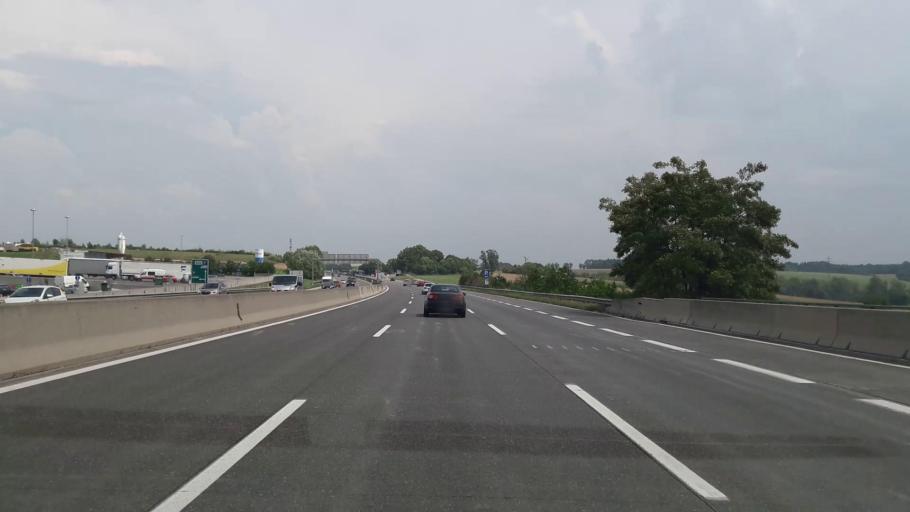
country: AT
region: Lower Austria
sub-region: Politischer Bezirk Amstetten
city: Zeillern
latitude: 48.1163
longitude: 14.7314
